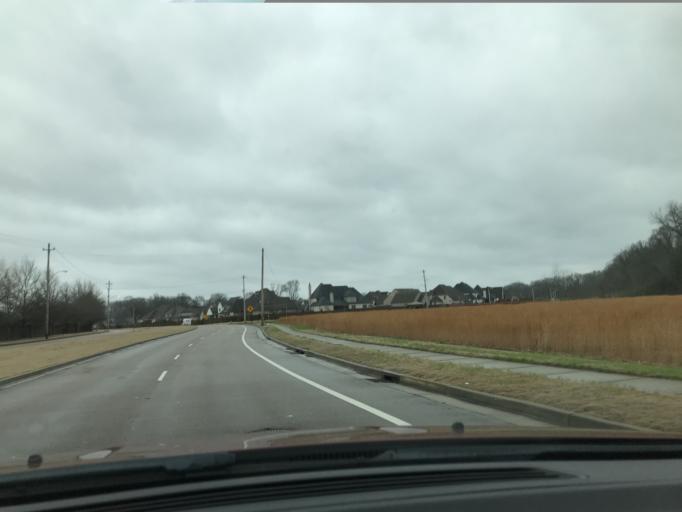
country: US
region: Tennessee
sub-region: Shelby County
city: Collierville
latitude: 35.0889
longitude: -89.7073
